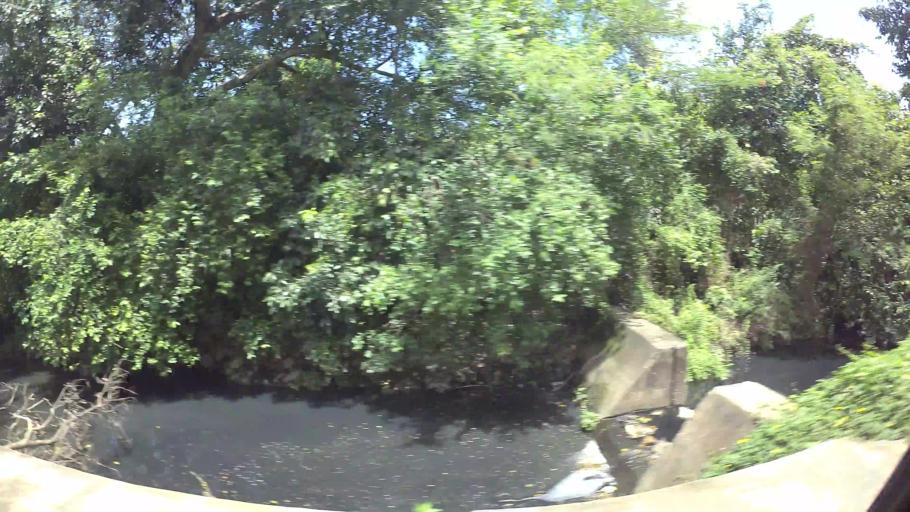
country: TH
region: Chon Buri
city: Sattahip
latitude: 12.7139
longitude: 100.8863
